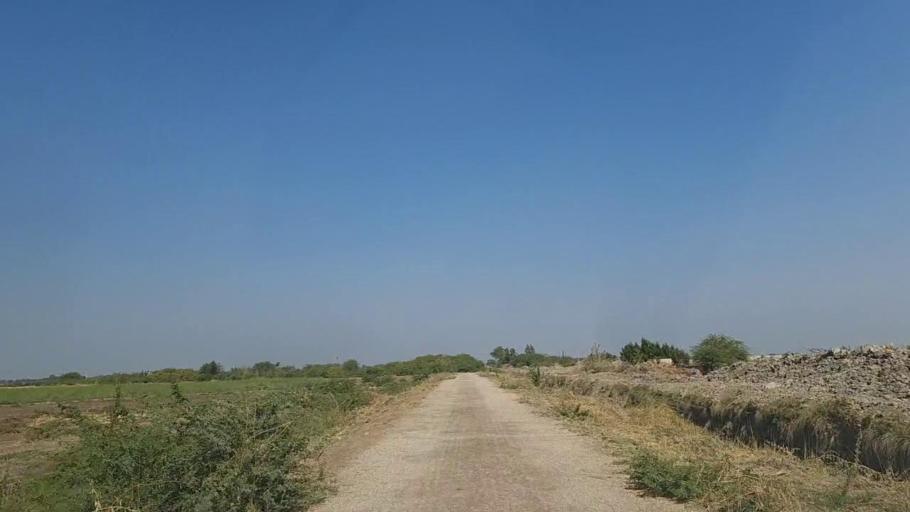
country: PK
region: Sindh
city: Digri
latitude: 25.1893
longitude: 69.1451
